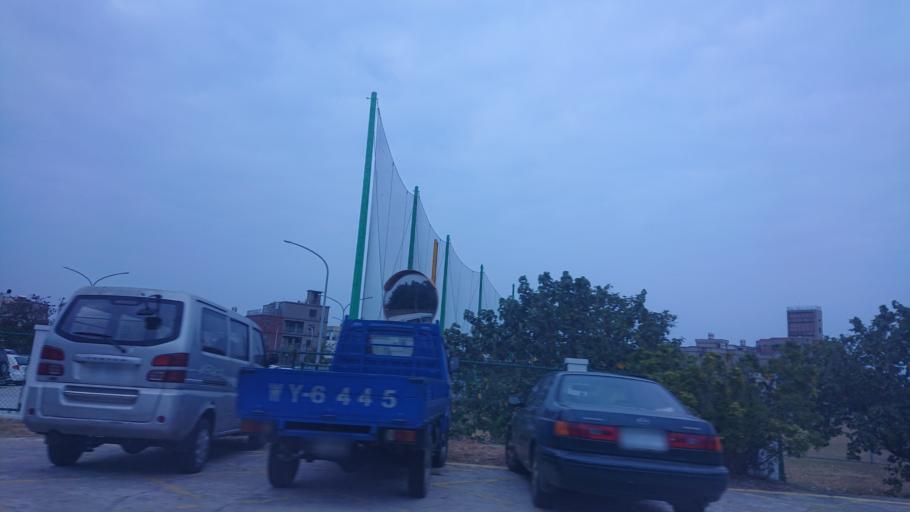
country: TW
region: Fukien
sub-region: Kinmen
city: Jincheng
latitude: 24.4346
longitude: 118.3136
